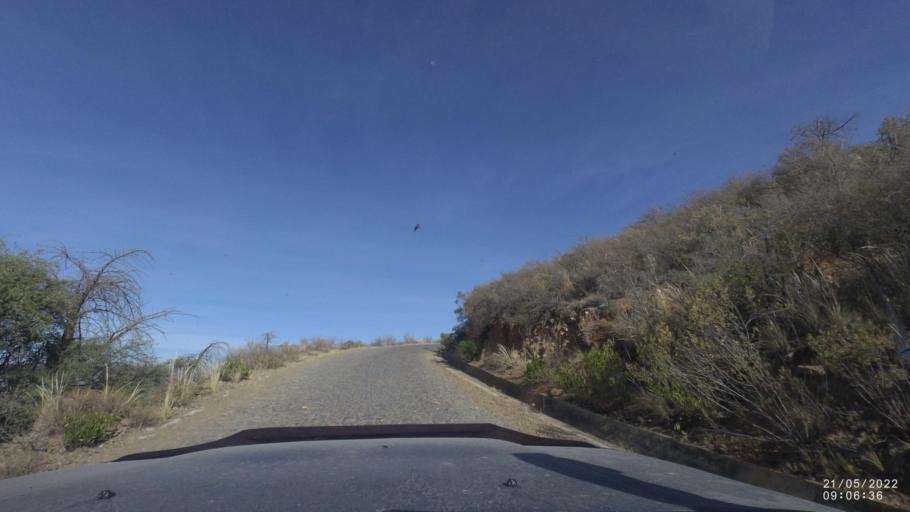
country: BO
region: Cochabamba
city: Cochabamba
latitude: -17.3777
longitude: -66.0231
